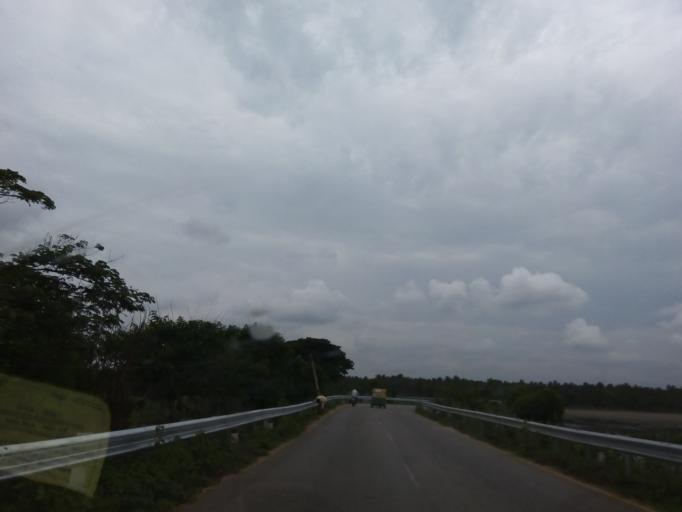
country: IN
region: Karnataka
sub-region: Hassan
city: Channarayapatna
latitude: 12.8800
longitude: 76.4228
